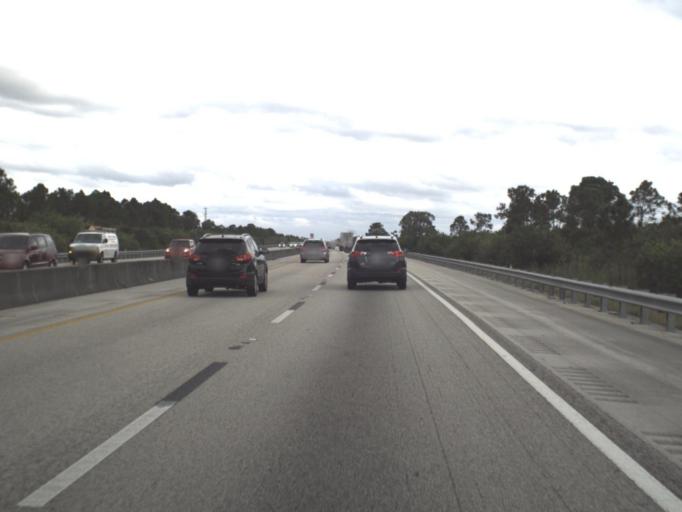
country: US
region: Florida
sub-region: Martin County
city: Hobe Sound
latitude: 27.0265
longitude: -80.2327
